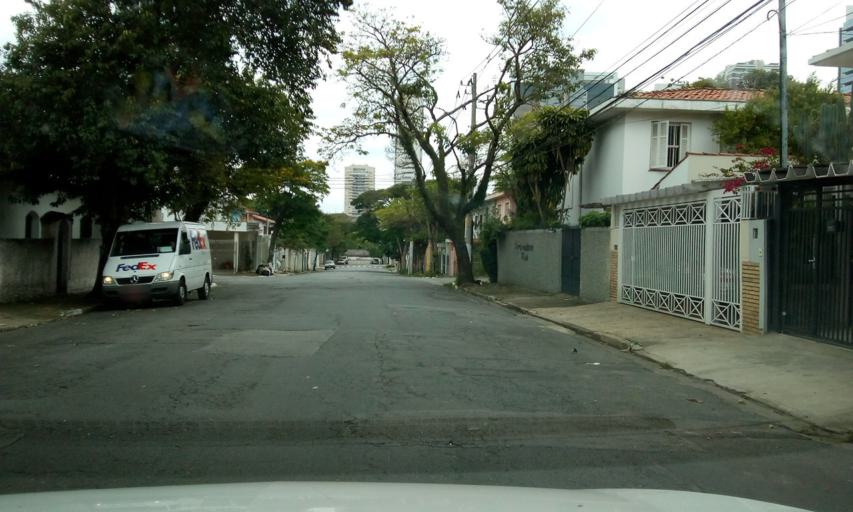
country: BR
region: Sao Paulo
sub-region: Sao Paulo
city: Sao Paulo
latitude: -23.6177
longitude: -46.6901
